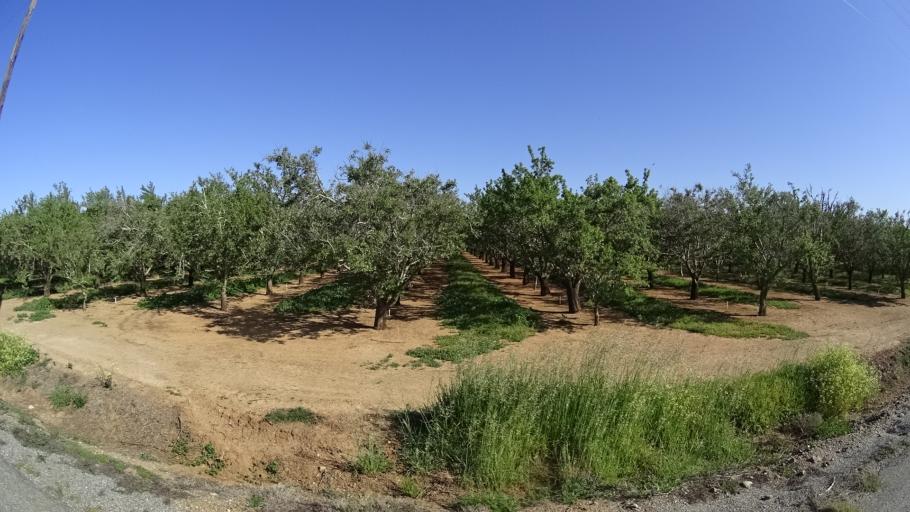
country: US
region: California
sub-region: Glenn County
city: Hamilton City
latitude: 39.7756
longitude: -122.0701
